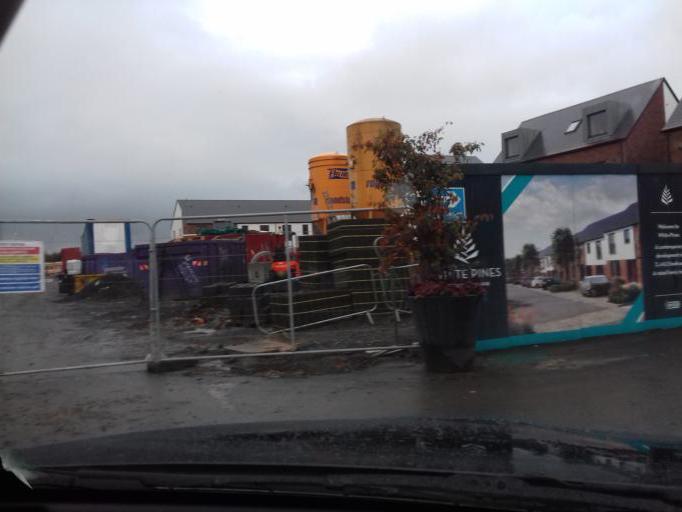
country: IE
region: Leinster
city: Ballyboden
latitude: 53.2741
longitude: -6.3147
